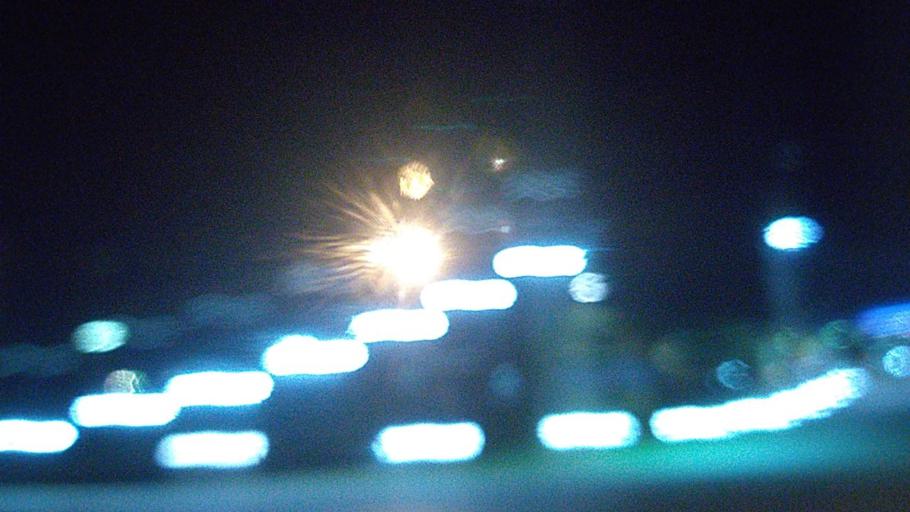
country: TH
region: Ang Thong
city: Chaiyo
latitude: 14.7325
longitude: 100.4549
